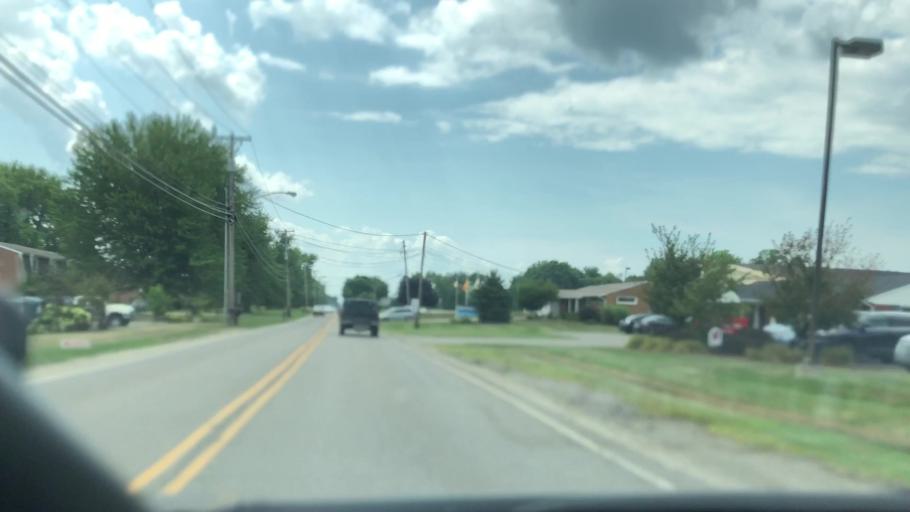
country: US
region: Ohio
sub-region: Summit County
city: Greensburg
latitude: 40.8790
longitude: -81.4843
